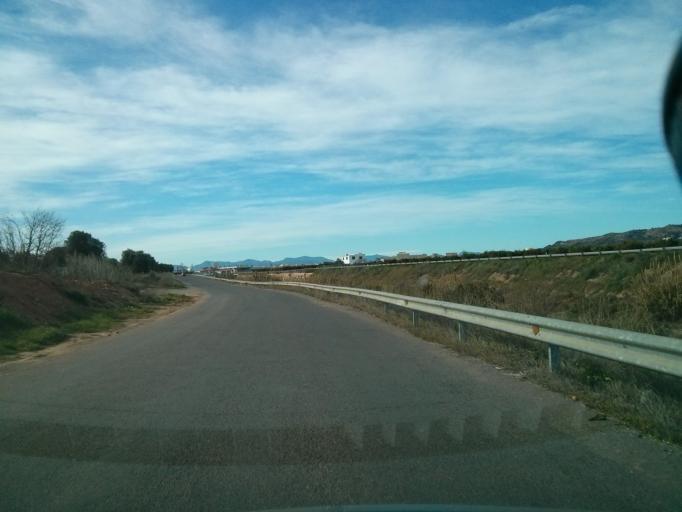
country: ES
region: Valencia
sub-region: Provincia de Castello
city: Castello de la Plana
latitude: 40.0048
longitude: -0.0258
